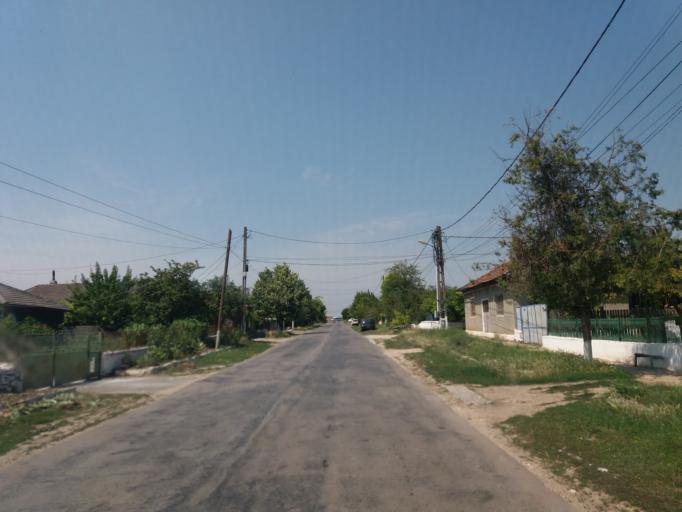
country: RO
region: Constanta
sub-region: Comuna Corbu
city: Corbu
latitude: 44.4209
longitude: 28.6606
